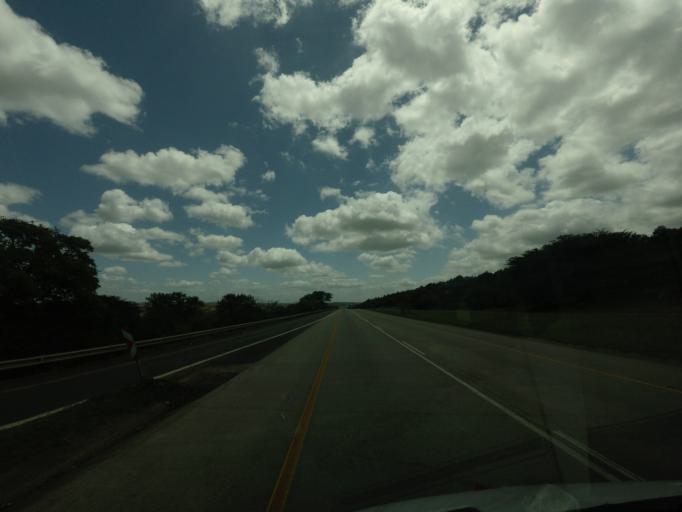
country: ZA
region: KwaZulu-Natal
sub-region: uMkhanyakude District Municipality
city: Mtubatuba
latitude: -28.4691
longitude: 32.1465
